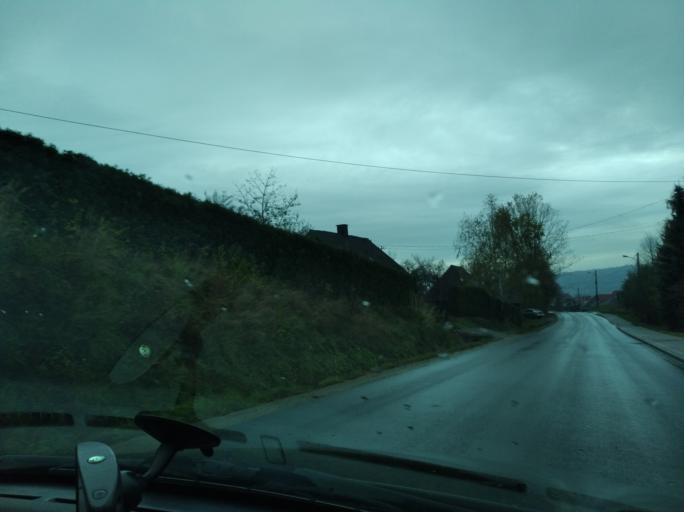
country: PL
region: Subcarpathian Voivodeship
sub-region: Powiat rzeszowski
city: Tyczyn
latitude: 49.9462
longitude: 22.0386
